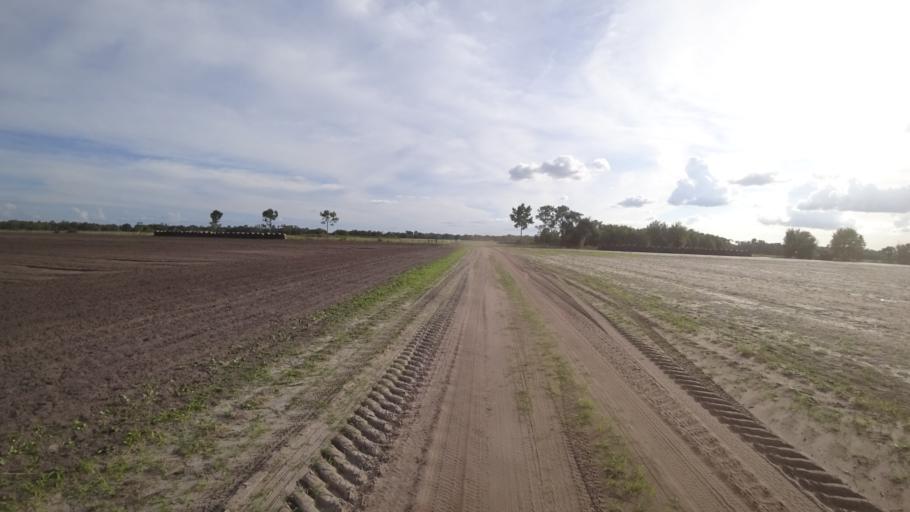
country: US
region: Florida
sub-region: Hillsborough County
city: Wimauma
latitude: 27.5603
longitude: -82.0955
